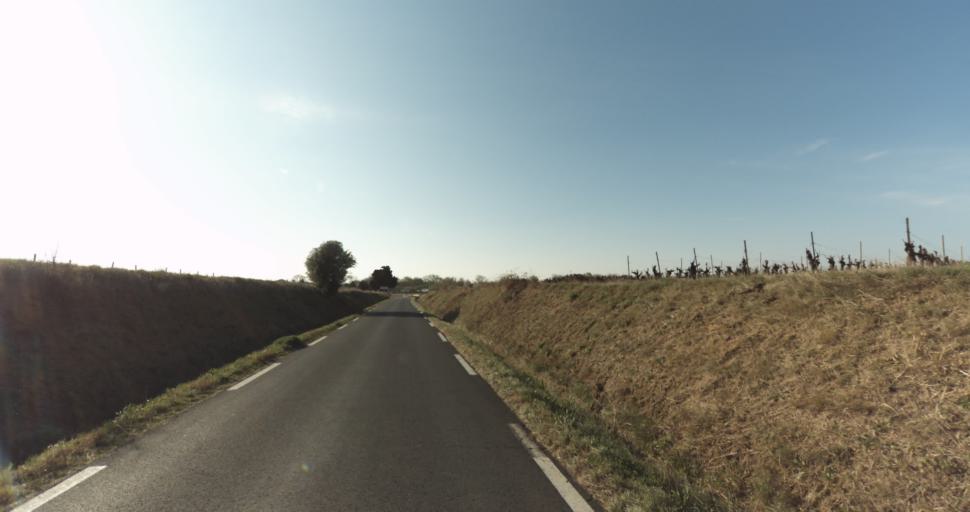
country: FR
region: Languedoc-Roussillon
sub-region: Departement de l'Herault
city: Pomerols
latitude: 43.3755
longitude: 3.5154
